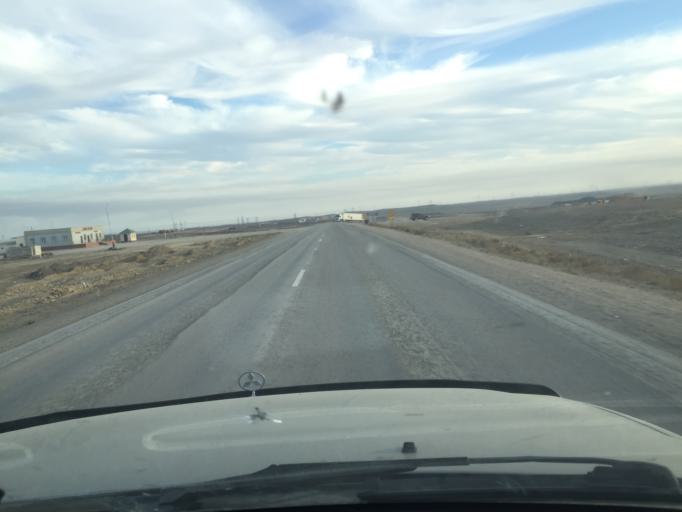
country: KZ
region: Almaty Oblysy
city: Ulken
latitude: 45.1597
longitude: 73.9449
